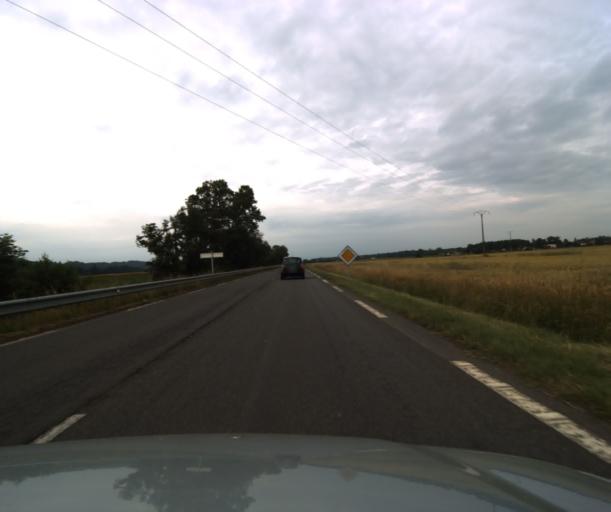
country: FR
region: Midi-Pyrenees
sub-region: Departement des Hautes-Pyrenees
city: Rabastens-de-Bigorre
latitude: 43.3542
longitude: 0.1381
